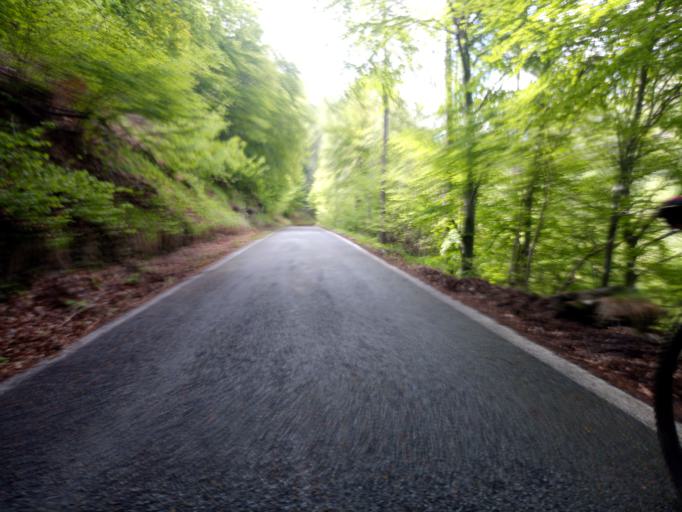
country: IT
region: Piedmont
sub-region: Provincia di Torino
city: Meana di Susa
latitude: 45.1043
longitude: 7.0653
